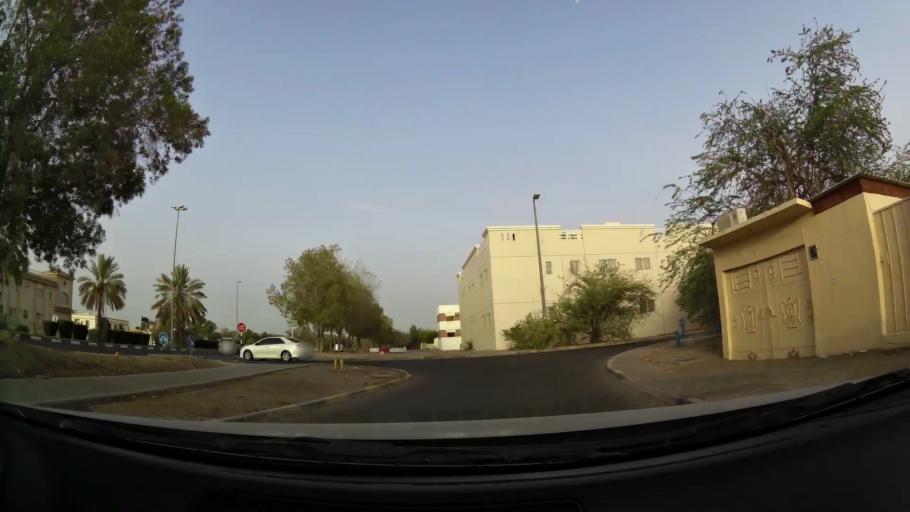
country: OM
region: Al Buraimi
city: Al Buraymi
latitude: 24.2471
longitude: 55.7341
